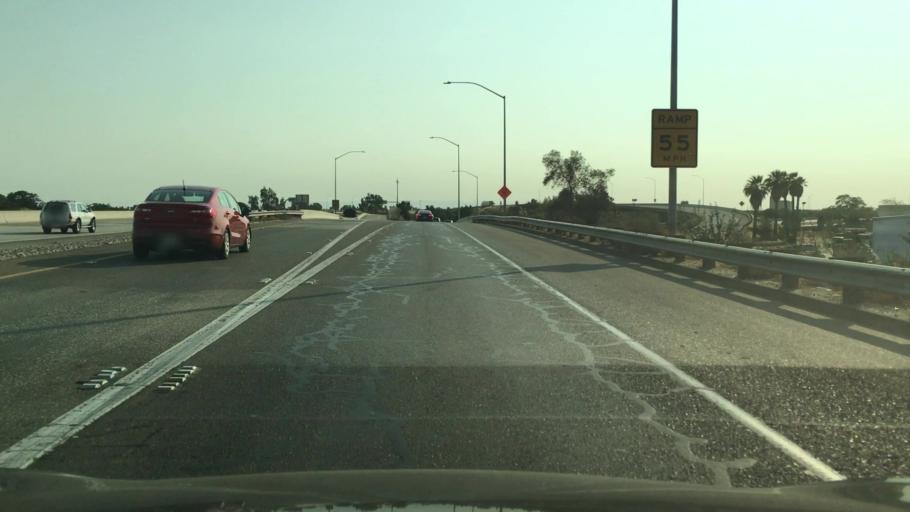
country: US
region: California
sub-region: Fresno County
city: Fresno
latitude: 36.7425
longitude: -119.8125
